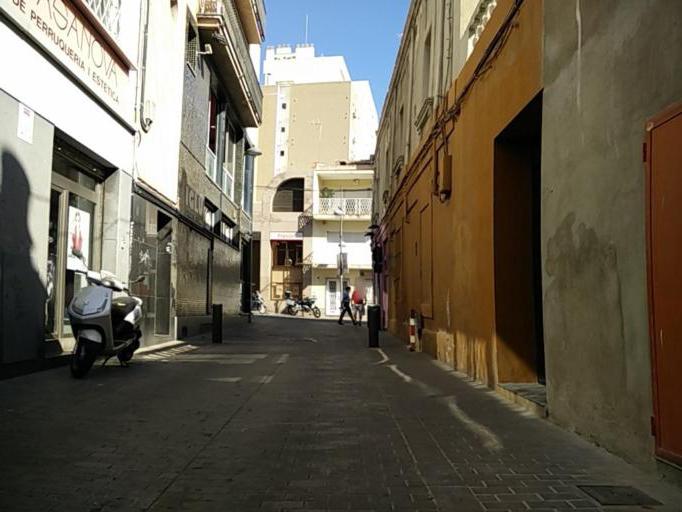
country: ES
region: Catalonia
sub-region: Provincia de Barcelona
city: Badalona
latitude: 41.4492
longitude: 2.2463
